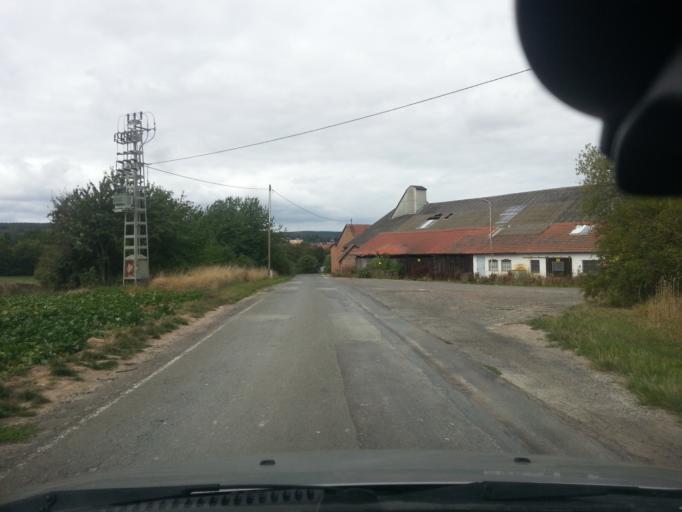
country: DE
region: Rheinland-Pfalz
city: Eisenberg
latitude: 49.5546
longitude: 8.0796
